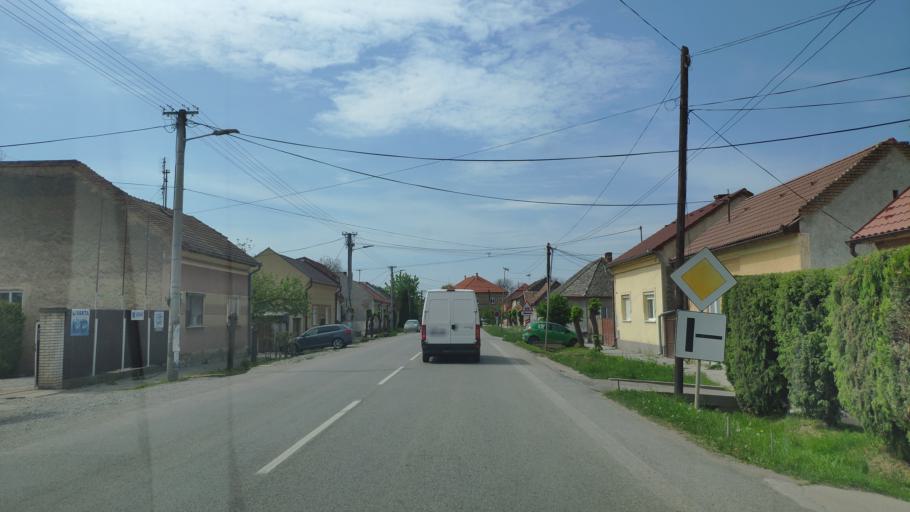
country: HU
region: Borsod-Abauj-Zemplen
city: Putnok
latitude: 48.4260
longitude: 20.3302
